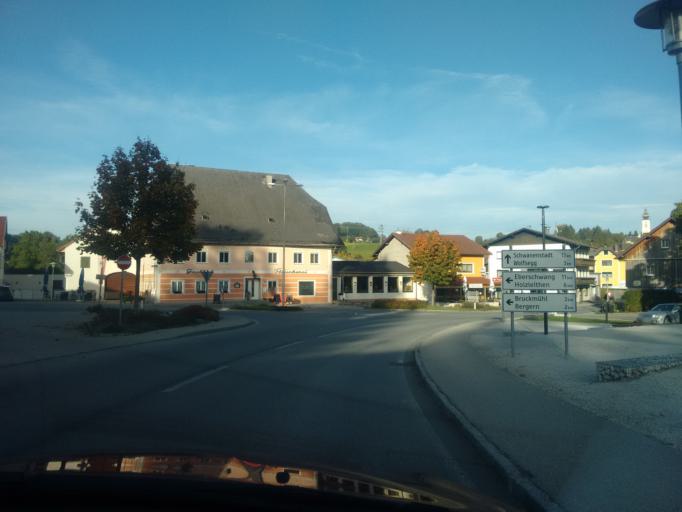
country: AT
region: Upper Austria
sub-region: Politischer Bezirk Vocklabruck
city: Manning
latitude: 48.0961
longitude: 13.6587
